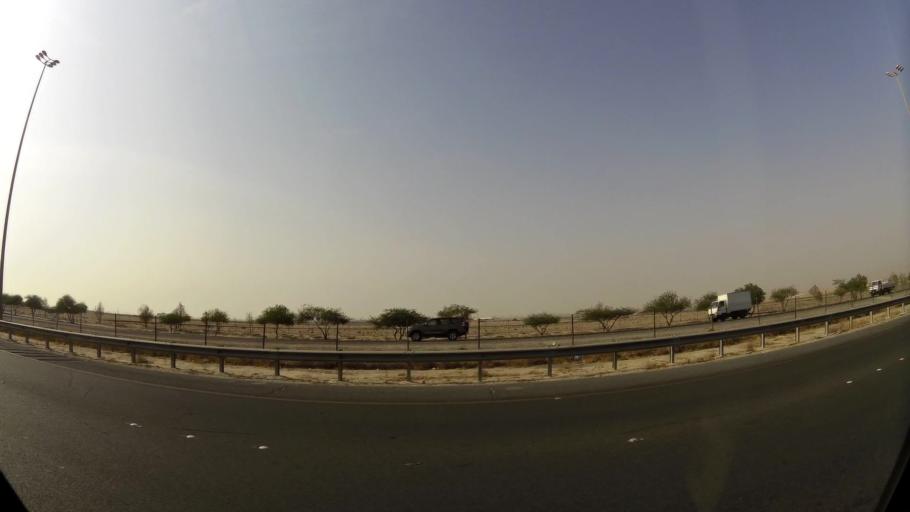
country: KW
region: Mubarak al Kabir
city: Mubarak al Kabir
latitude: 29.1798
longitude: 48.0297
